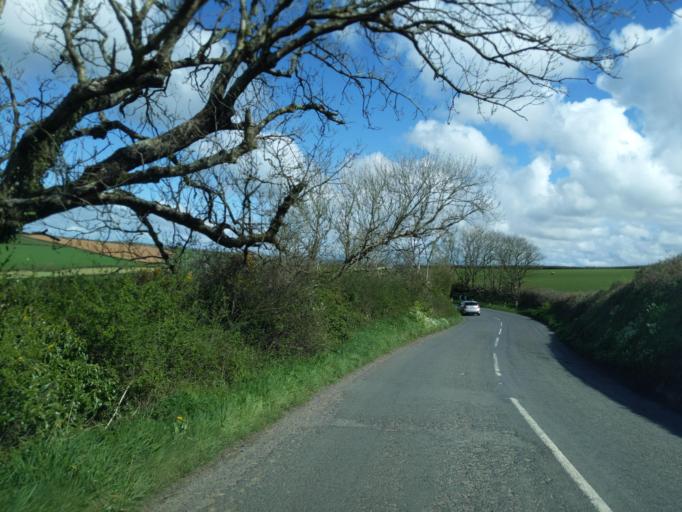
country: GB
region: England
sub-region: Cornwall
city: Wadebridge
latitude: 50.5741
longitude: -4.8203
